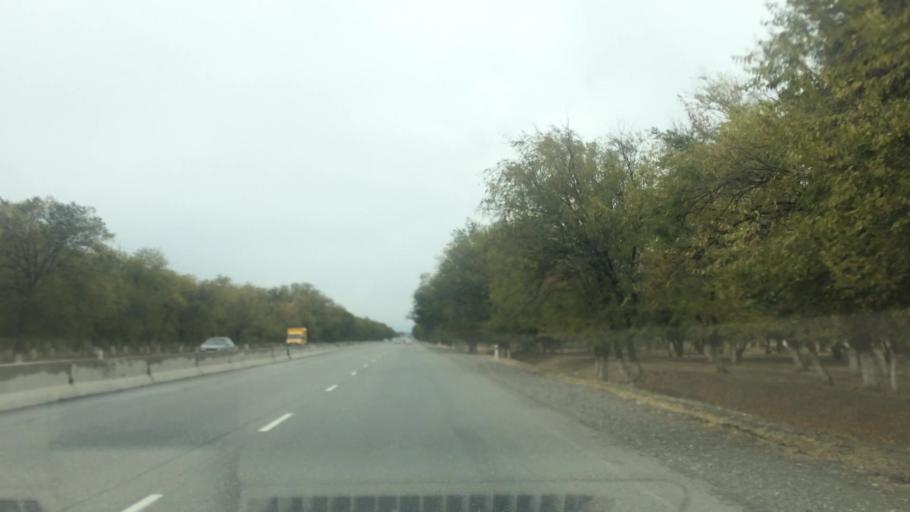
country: UZ
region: Samarqand
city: Bulung'ur
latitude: 39.7989
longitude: 67.3390
